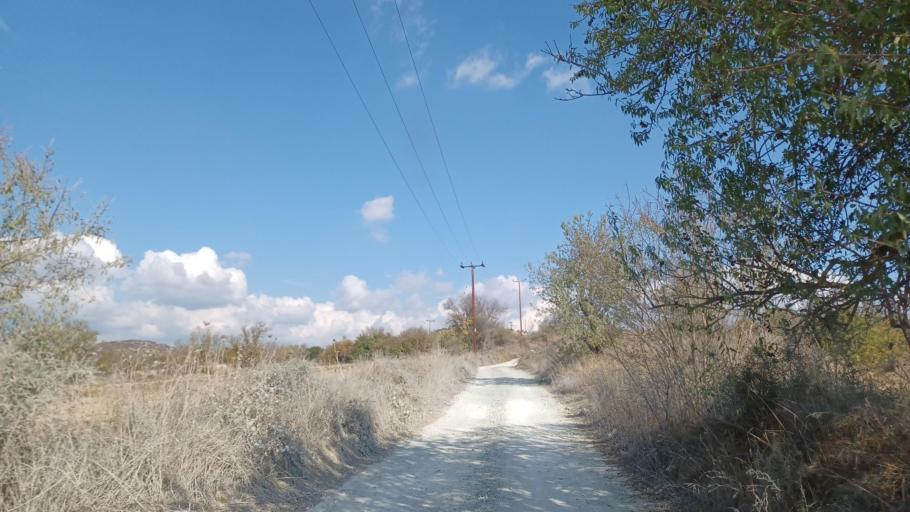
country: CY
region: Pafos
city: Mesogi
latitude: 34.8362
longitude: 32.5655
